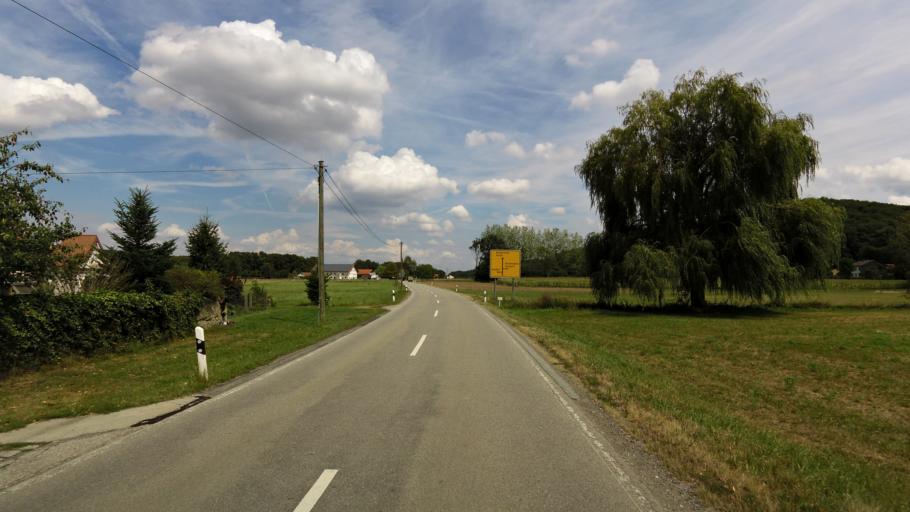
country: DE
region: Bavaria
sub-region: Upper Bavaria
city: Unterneukirchen
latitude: 48.1391
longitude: 12.6389
